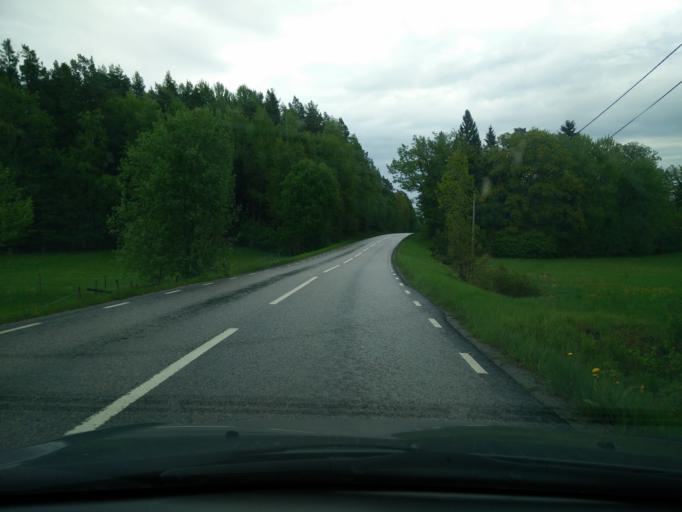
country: SE
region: Stockholm
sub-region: Norrtalje Kommun
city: Norrtalje
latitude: 59.7828
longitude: 18.8375
